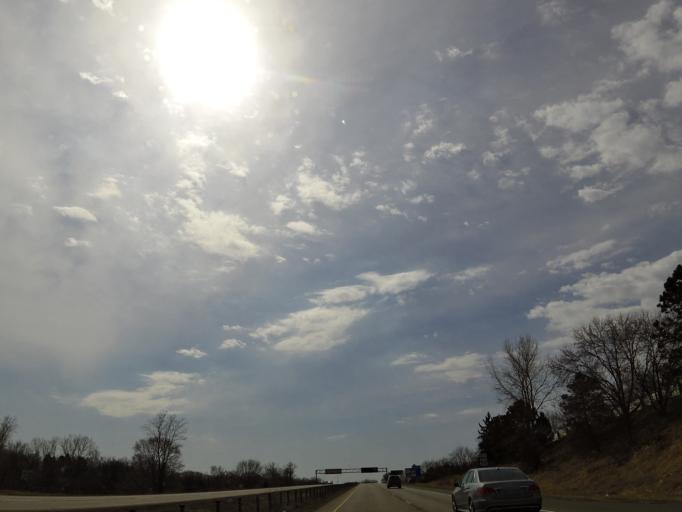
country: US
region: Minnesota
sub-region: Dakota County
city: South Saint Paul
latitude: 44.9009
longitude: -93.0658
